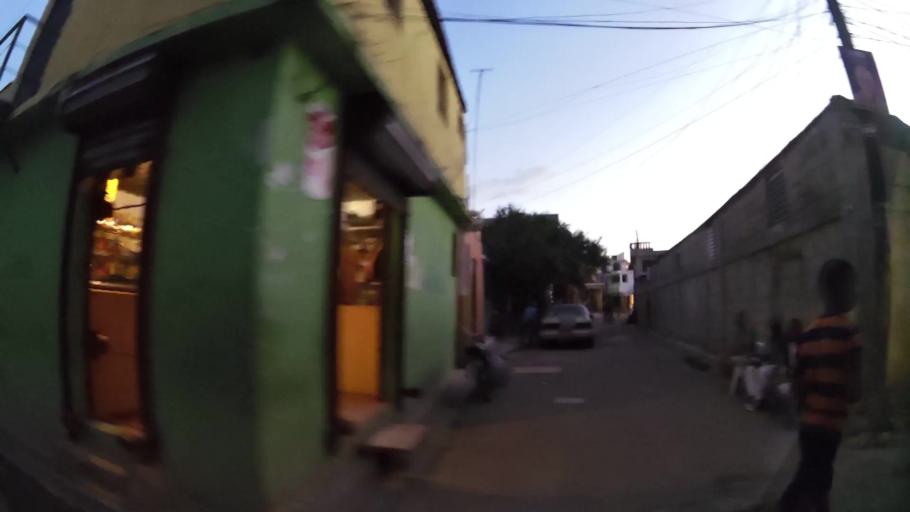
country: DO
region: Santo Domingo
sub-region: Santo Domingo
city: Santo Domingo Este
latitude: 18.5032
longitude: -69.8381
